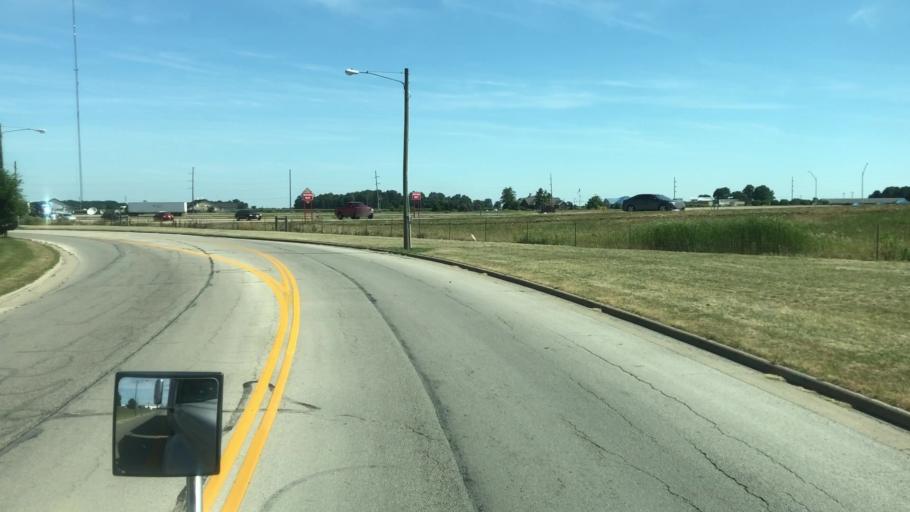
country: US
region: Ohio
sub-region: Sandusky County
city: Fremont
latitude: 41.3622
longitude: -83.0890
